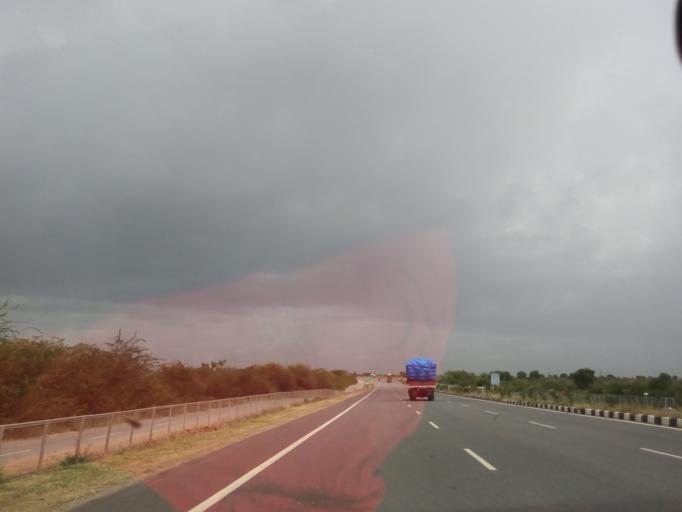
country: IN
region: Karnataka
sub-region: Chitradurga
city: Chitradurga
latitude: 14.1441
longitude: 76.4899
